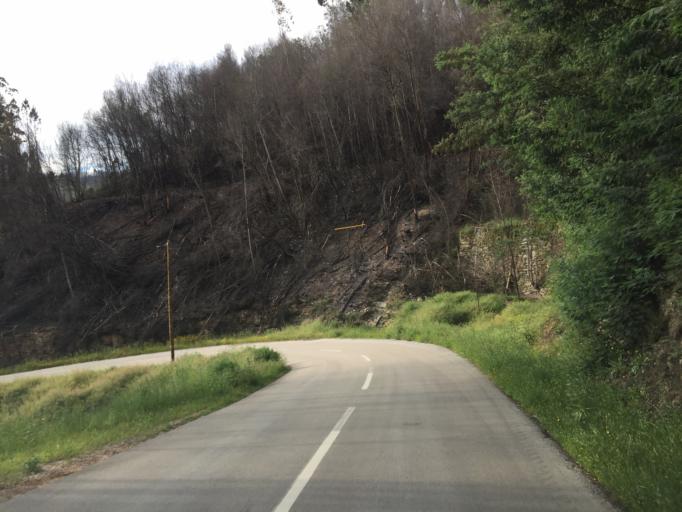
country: PT
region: Coimbra
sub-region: Arganil
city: Arganil
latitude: 40.1435
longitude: -8.0100
